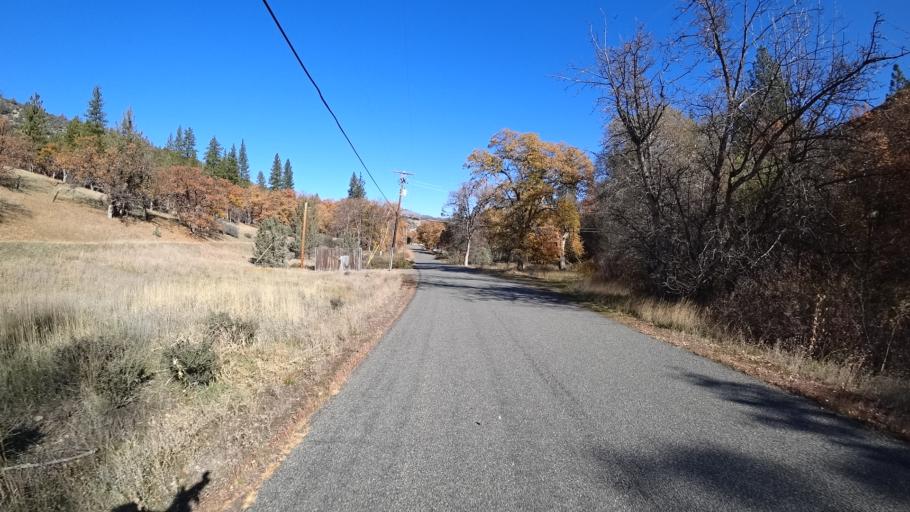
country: US
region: California
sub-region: Siskiyou County
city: Montague
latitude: 41.9694
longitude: -122.3038
